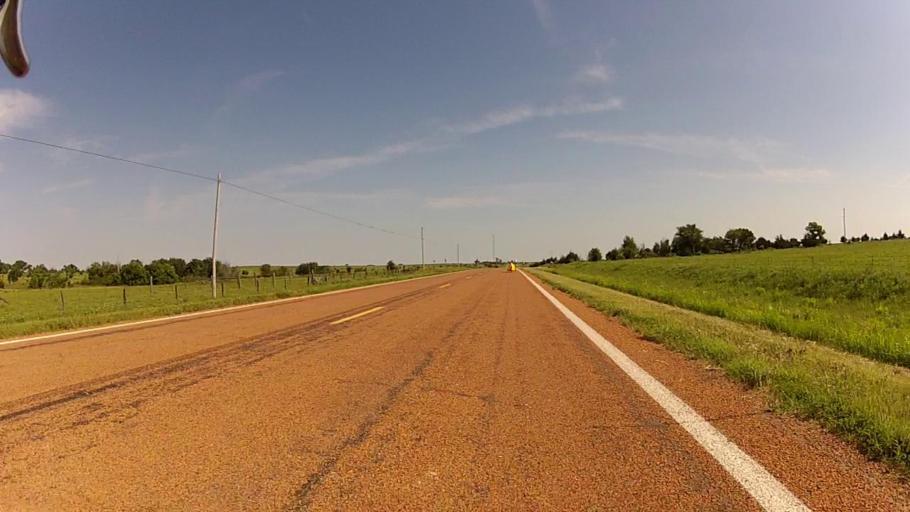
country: US
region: Kansas
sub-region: Cowley County
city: Winfield
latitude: 37.0993
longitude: -96.6436
